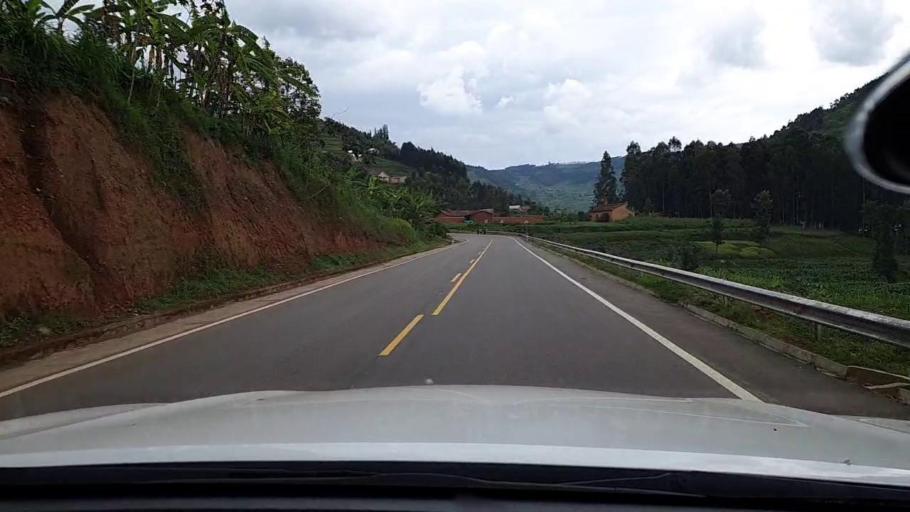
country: RW
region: Northern Province
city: Byumba
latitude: -1.6299
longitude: 29.9274
